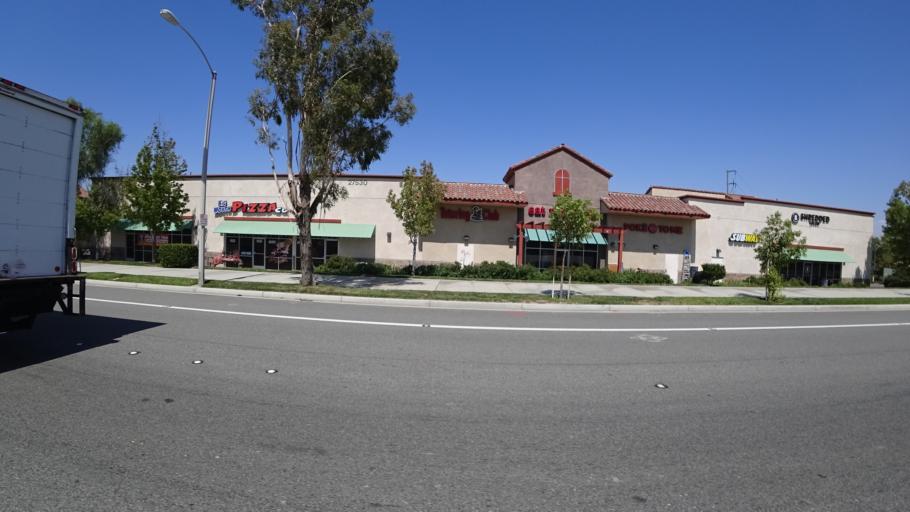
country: US
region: California
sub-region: Los Angeles County
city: Valencia
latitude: 34.4358
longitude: -118.5630
